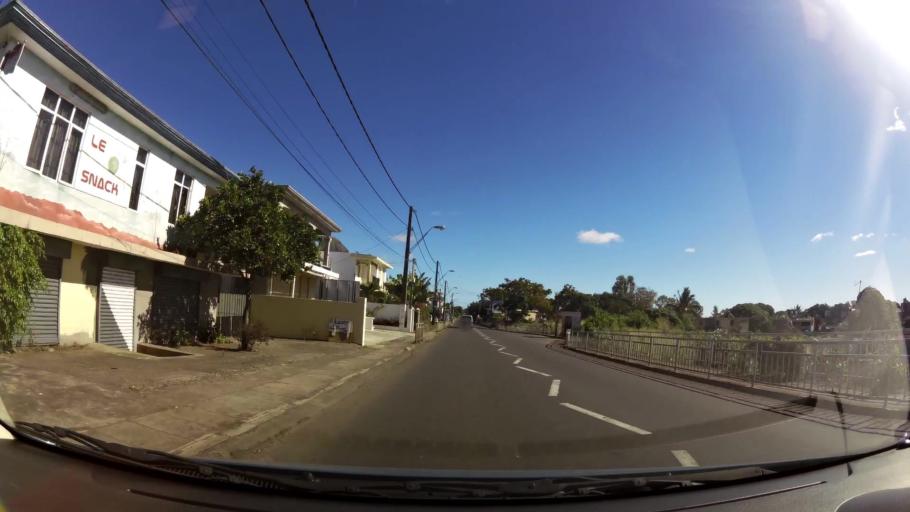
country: MU
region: Plaines Wilhems
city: Vacoas
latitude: -20.2820
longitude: 57.4522
